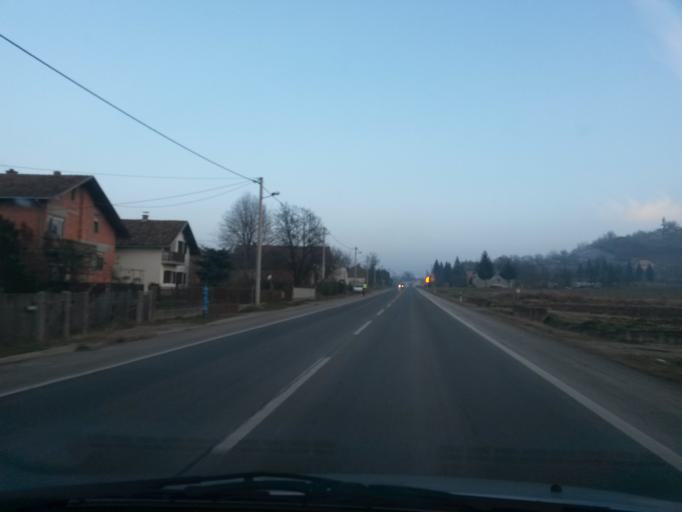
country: HR
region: Varazdinska
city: Ludbreg
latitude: 46.2388
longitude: 16.6358
